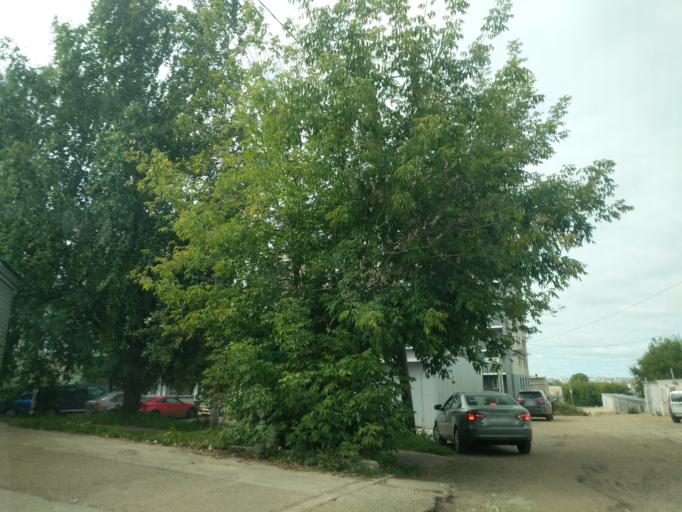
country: RU
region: Kirov
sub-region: Kirovo-Chepetskiy Rayon
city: Kirov
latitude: 58.5978
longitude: 49.6455
